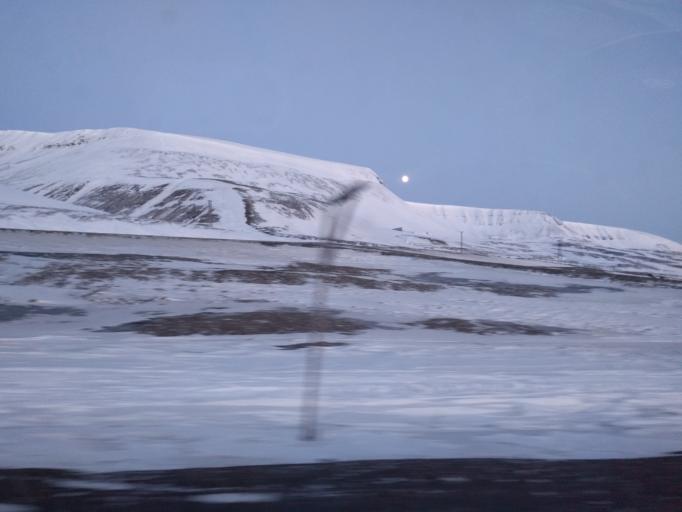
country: SJ
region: Svalbard
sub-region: Spitsbergen
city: Longyearbyen
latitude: 78.2391
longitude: 15.5220
